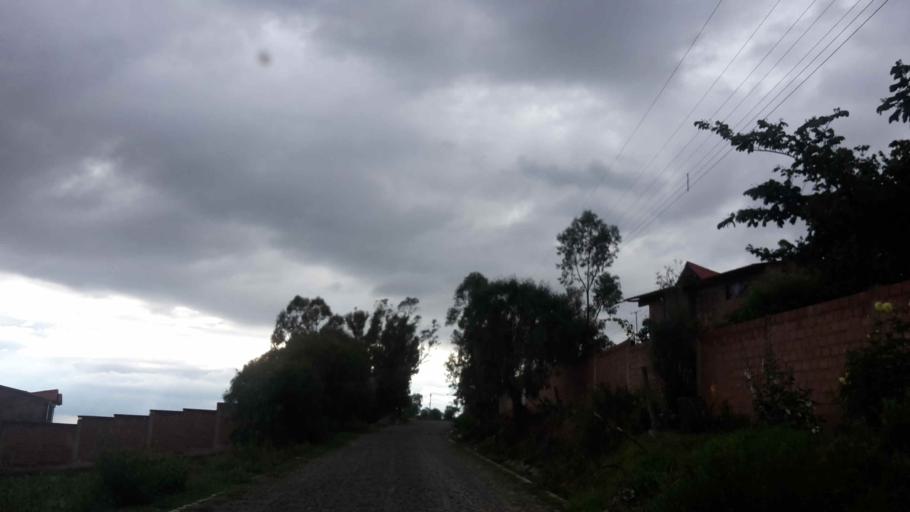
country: BO
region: Cochabamba
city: Cochabamba
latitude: -17.3733
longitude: -66.0570
